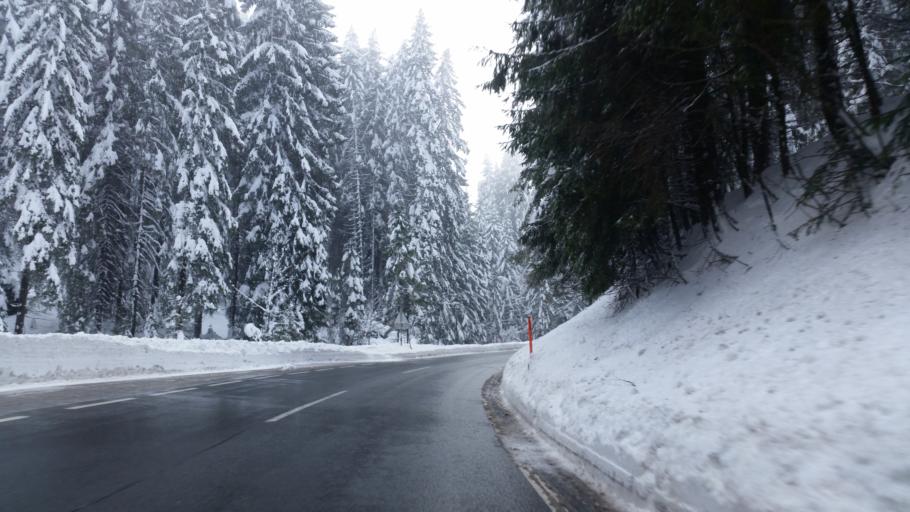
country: AT
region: Salzburg
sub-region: Politischer Bezirk Sankt Johann im Pongau
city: Eben im Pongau
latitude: 47.4795
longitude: 13.3928
